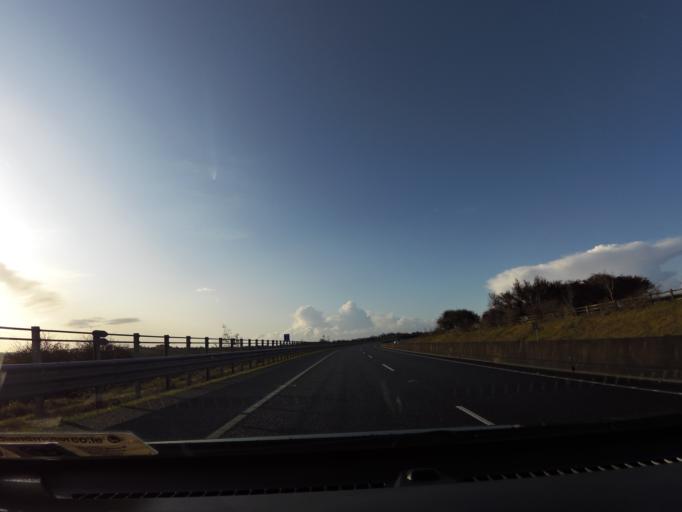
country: IE
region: Connaught
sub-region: County Galway
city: Gort
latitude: 53.0081
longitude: -8.8616
